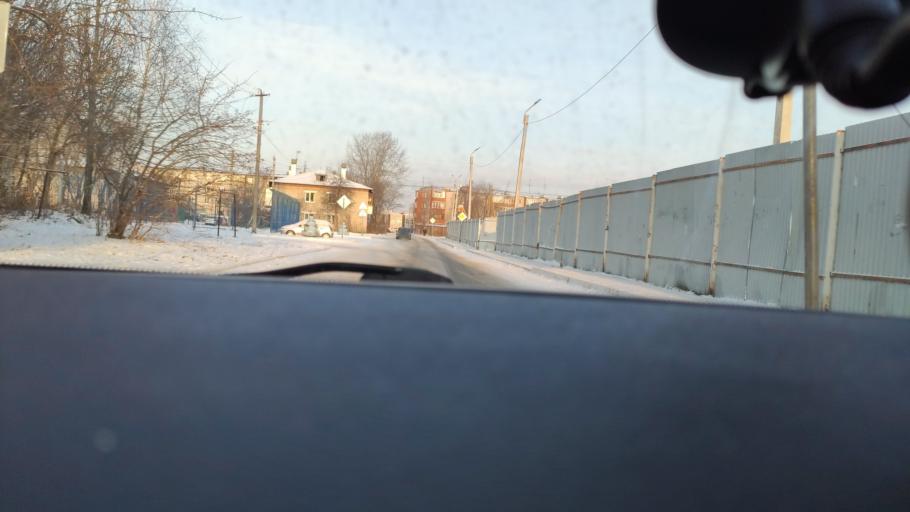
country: RU
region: Perm
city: Kondratovo
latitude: 57.9439
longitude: 56.0666
